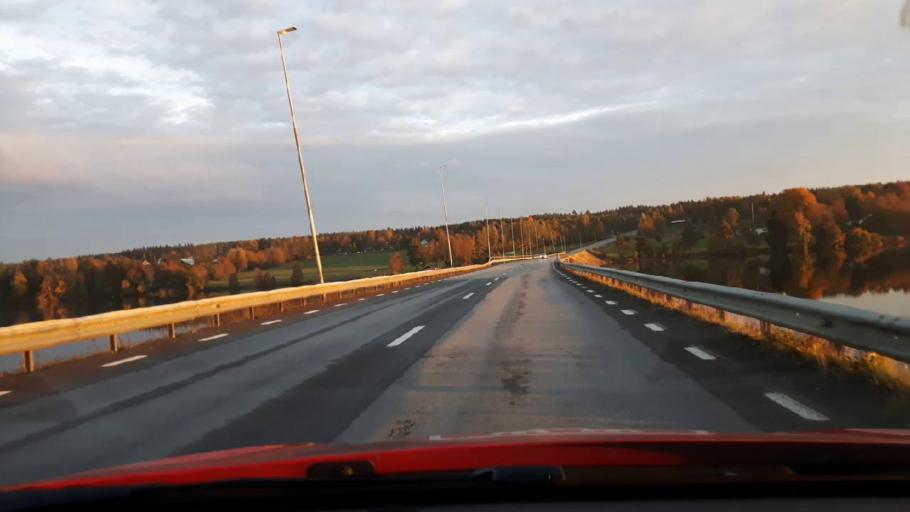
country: SE
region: Jaemtland
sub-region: OEstersunds Kommun
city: Lit
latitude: 63.3139
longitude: 14.8683
